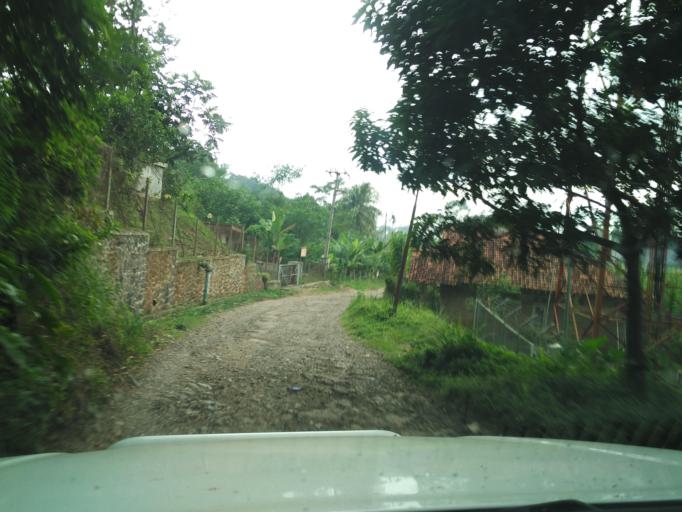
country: ID
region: West Java
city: Ciranjang-hilir
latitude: -6.6972
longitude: 107.1719
